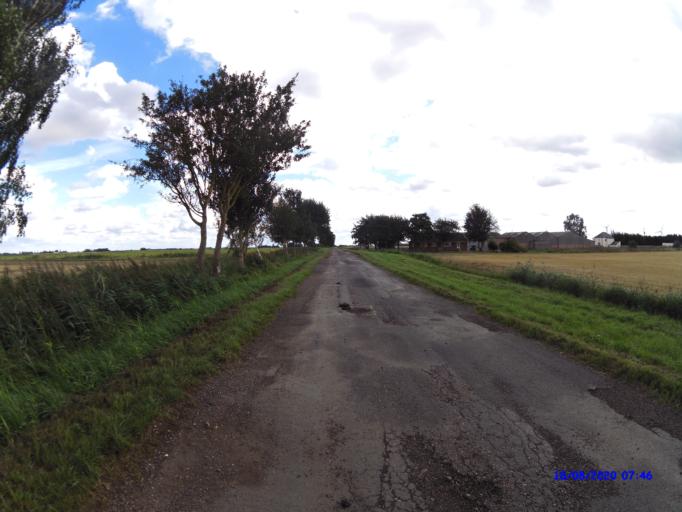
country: GB
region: England
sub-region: Cambridgeshire
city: Whittlesey
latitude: 52.5256
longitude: -0.1015
